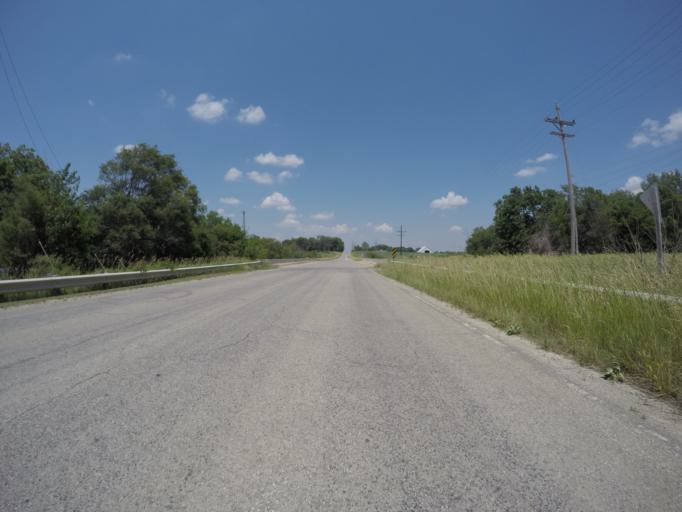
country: US
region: Kansas
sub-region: Doniphan County
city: Troy
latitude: 39.7723
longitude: -95.0969
